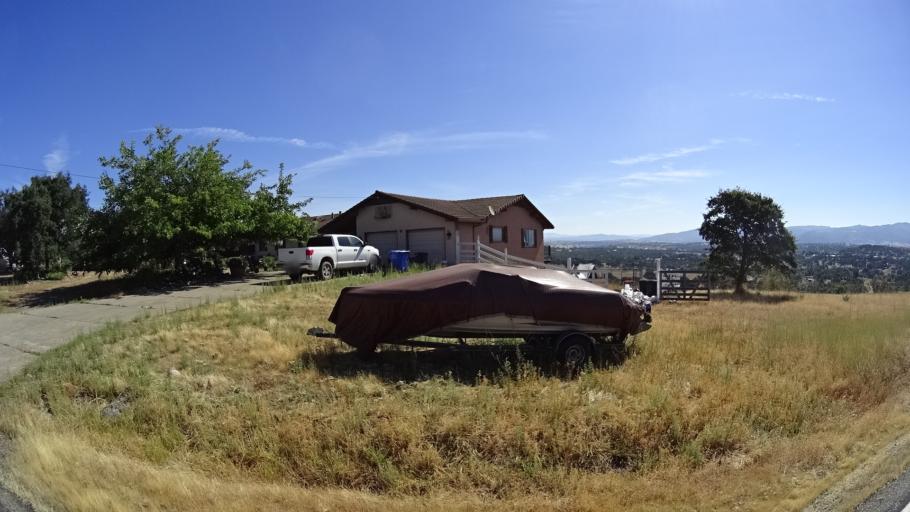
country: US
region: California
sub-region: Calaveras County
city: Valley Springs
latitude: 38.1709
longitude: -120.8612
